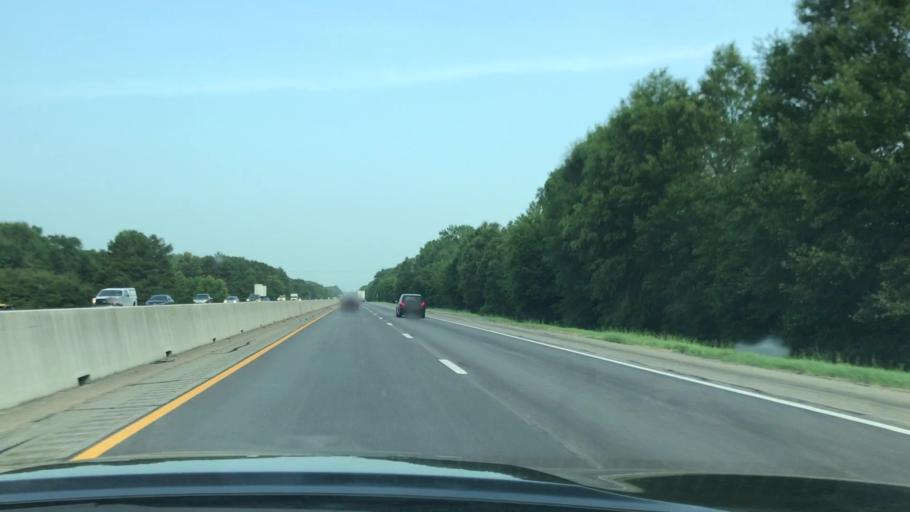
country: US
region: Texas
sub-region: Gregg County
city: Kilgore
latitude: 32.4326
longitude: -94.8788
